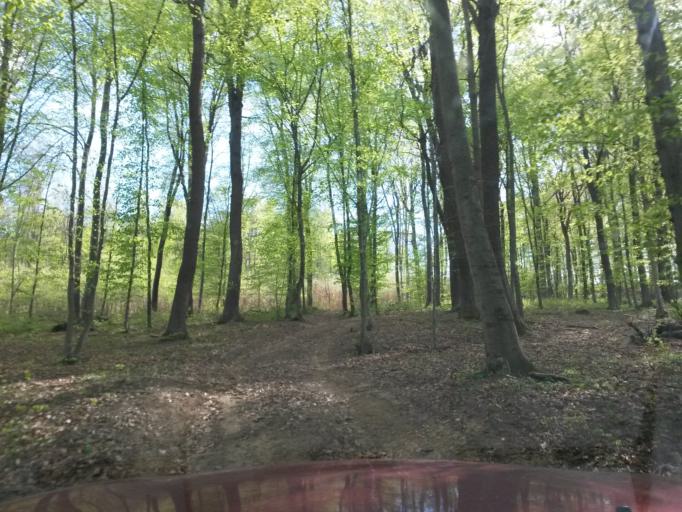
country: SK
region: Presovsky
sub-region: Okres Presov
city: Presov
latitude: 48.9553
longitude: 21.1327
